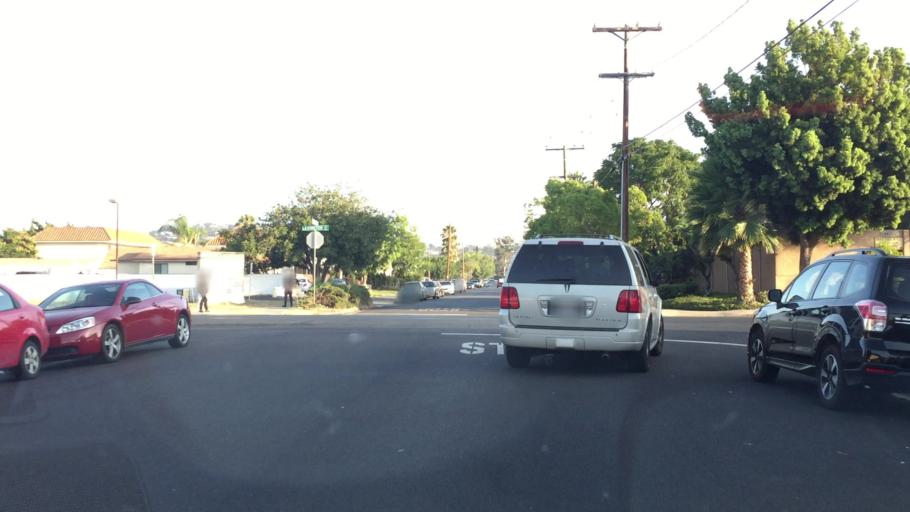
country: US
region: California
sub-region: San Diego County
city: El Cajon
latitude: 32.7930
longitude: -116.9588
